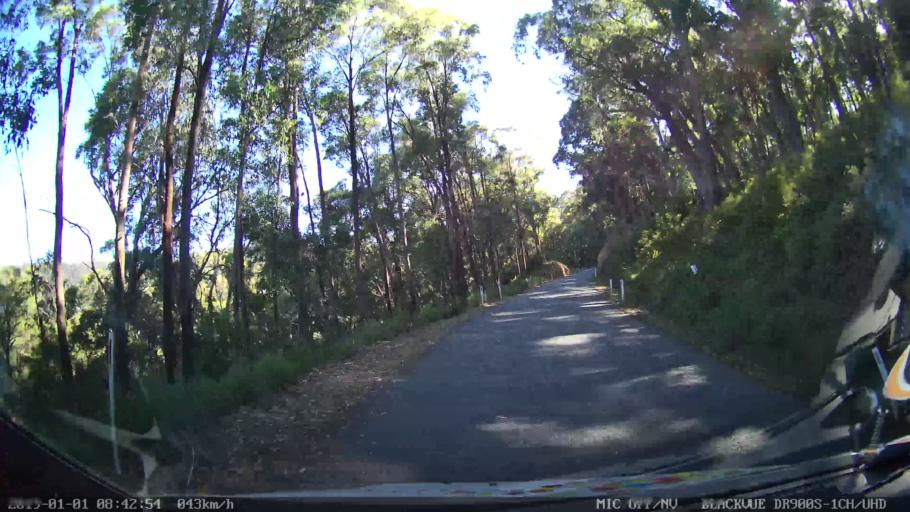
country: AU
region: New South Wales
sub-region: Snowy River
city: Jindabyne
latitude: -36.3206
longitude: 148.1920
